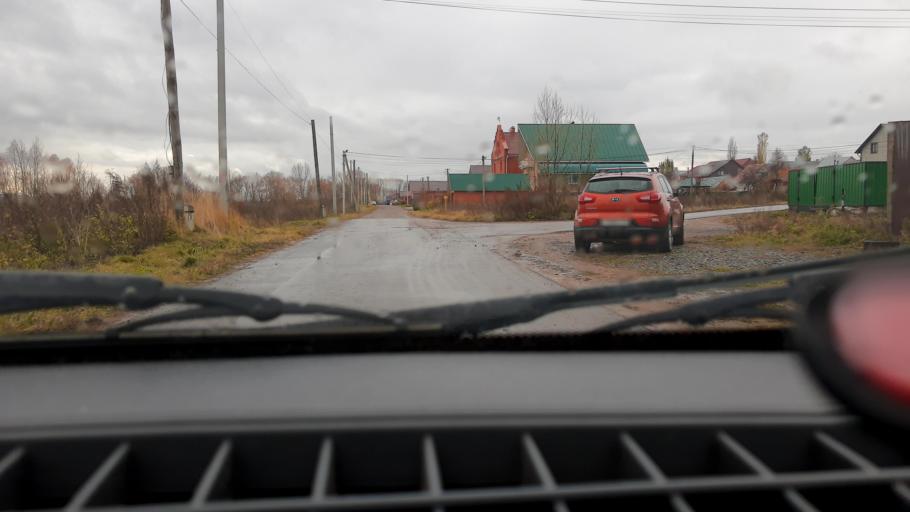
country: RU
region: Bashkortostan
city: Ufa
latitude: 54.8218
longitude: 55.9934
